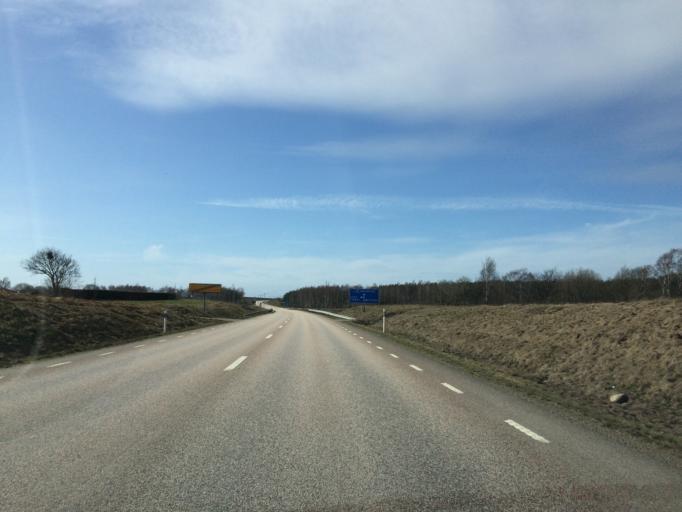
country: SE
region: Halland
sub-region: Laholms Kommun
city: Veinge
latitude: 56.5440
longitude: 13.0774
